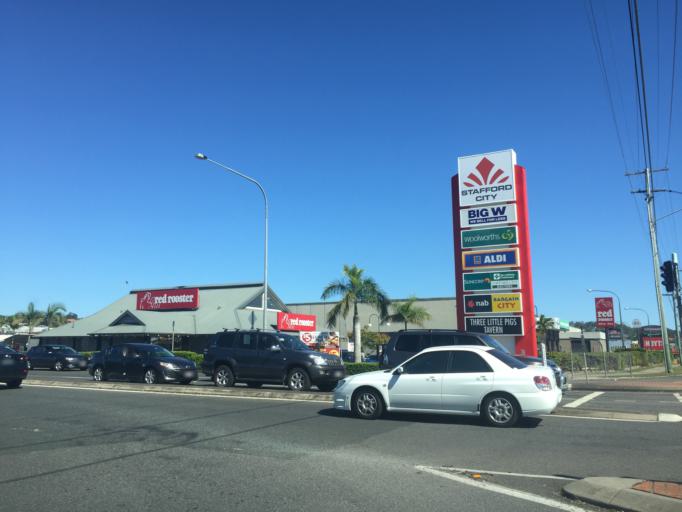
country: AU
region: Queensland
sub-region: Brisbane
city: Stafford
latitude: -27.4102
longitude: 153.0139
